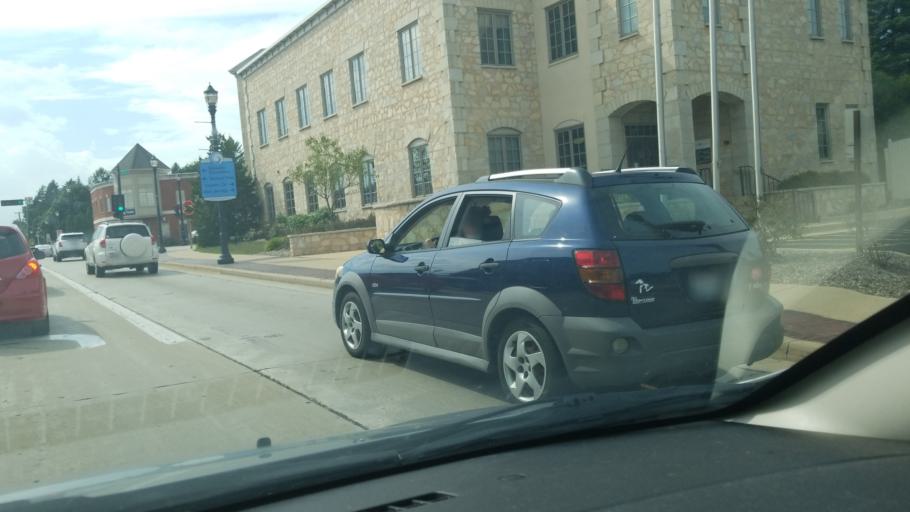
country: US
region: Wisconsin
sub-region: Ozaukee County
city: Grafton
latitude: 43.3200
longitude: -87.9509
